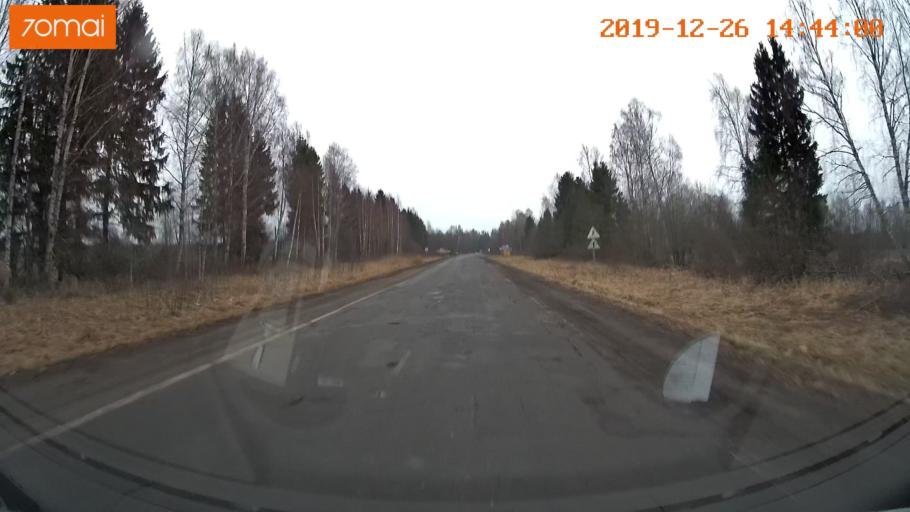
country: RU
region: Jaroslavl
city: Poshekhon'ye
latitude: 58.3519
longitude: 39.0462
